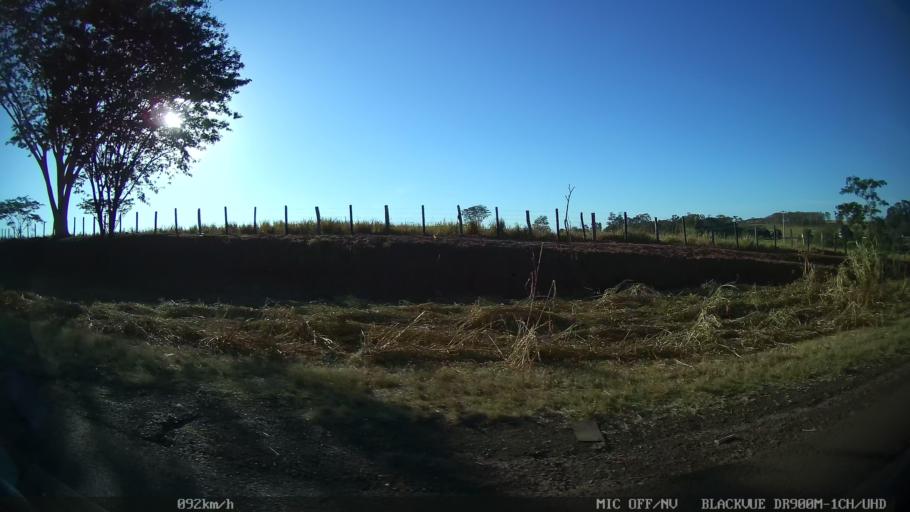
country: BR
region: Sao Paulo
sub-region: Guapiacu
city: Guapiacu
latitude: -20.7670
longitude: -49.2018
